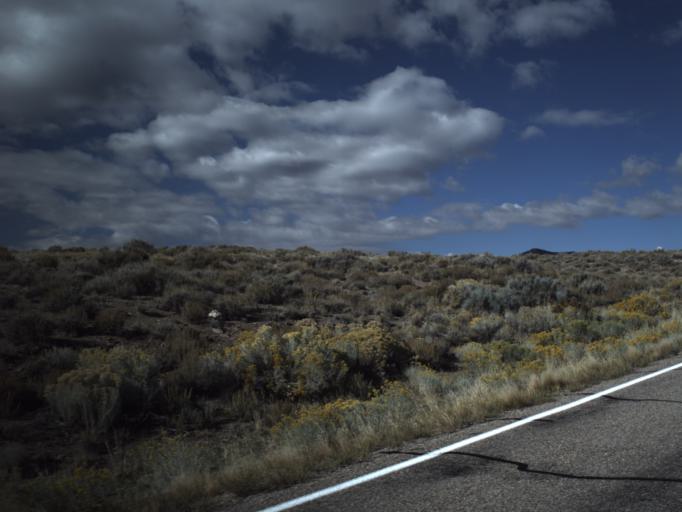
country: US
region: Utah
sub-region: Beaver County
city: Milford
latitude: 38.4520
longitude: -113.2034
